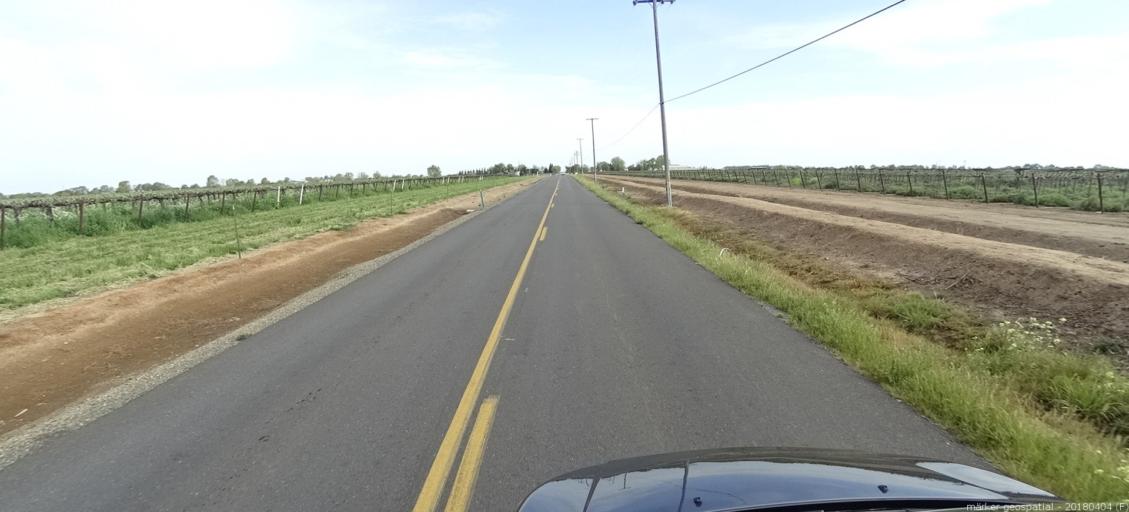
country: US
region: California
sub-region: Sacramento County
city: Galt
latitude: 38.3032
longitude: -121.3013
